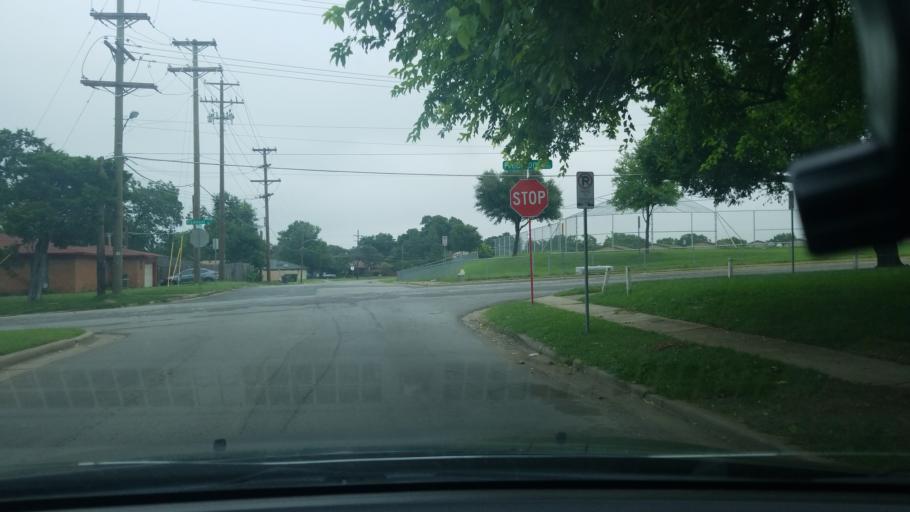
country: US
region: Texas
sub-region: Dallas County
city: Balch Springs
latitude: 32.7577
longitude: -96.6926
